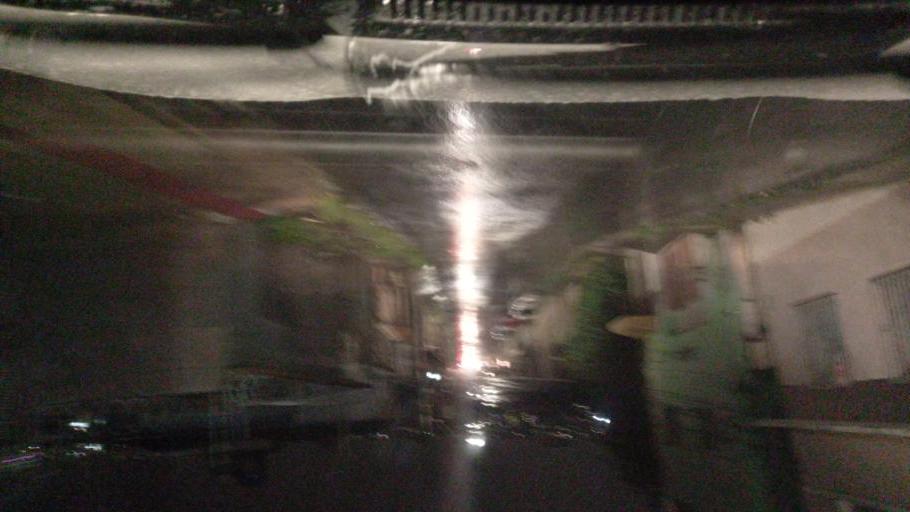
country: BR
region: Minas Gerais
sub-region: Belo Horizonte
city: Belo Horizonte
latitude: -19.9113
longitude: -43.9131
